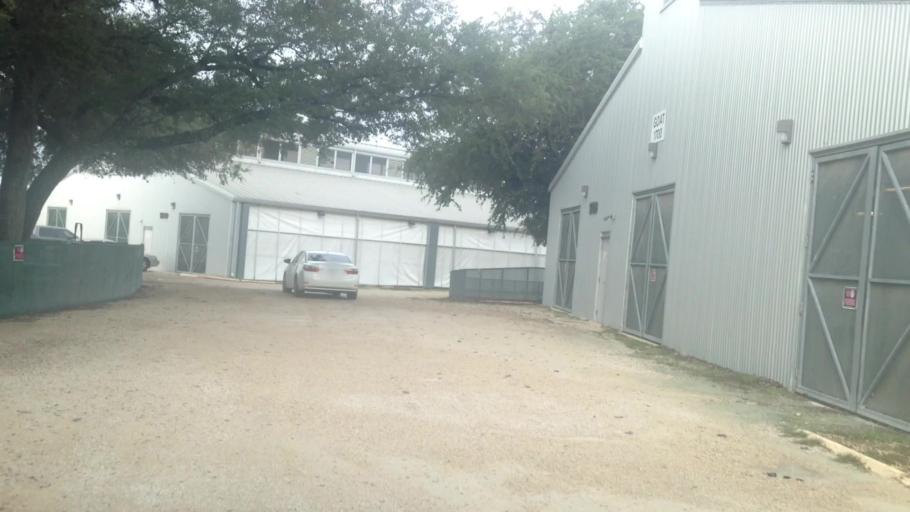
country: US
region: Texas
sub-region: Bexar County
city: Live Oak
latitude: 29.5859
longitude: -98.3917
